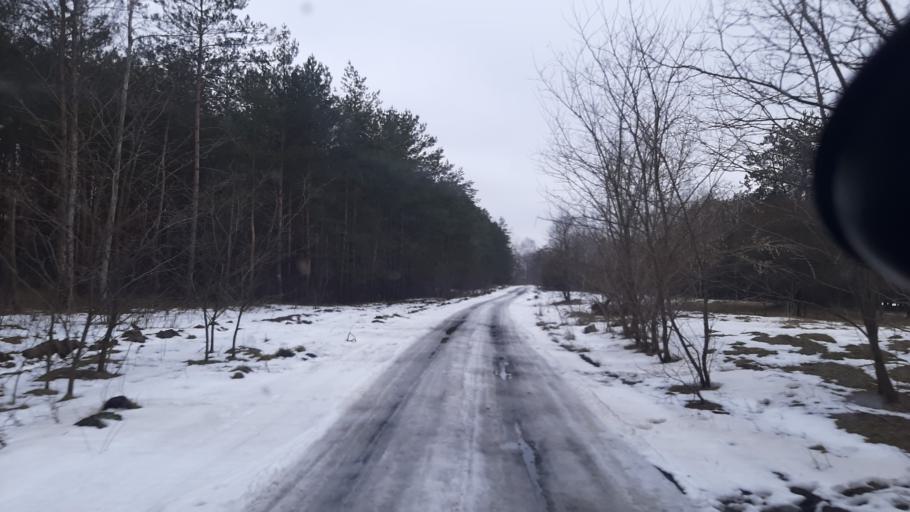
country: PL
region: Lublin Voivodeship
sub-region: Powiat wlodawski
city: Wlodawa
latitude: 51.5172
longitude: 23.5957
